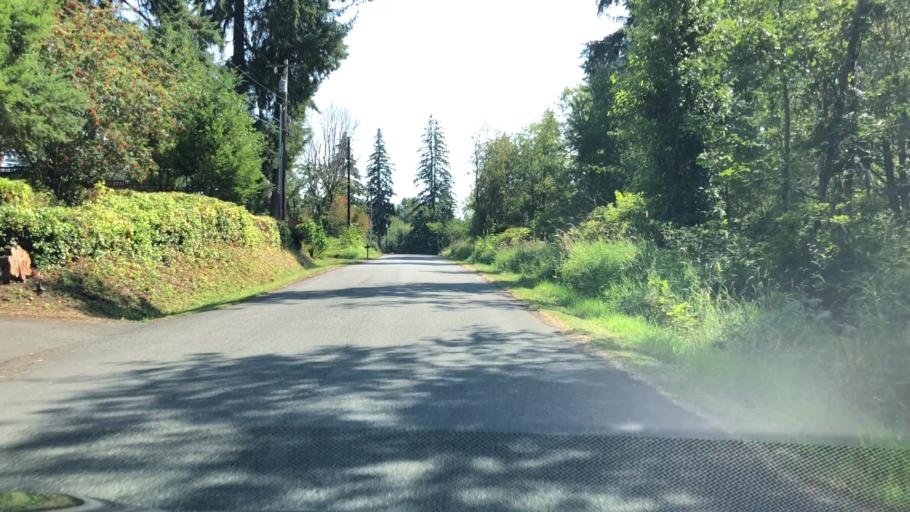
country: US
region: Washington
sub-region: Snohomish County
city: Maltby
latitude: 47.7821
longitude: -122.1371
